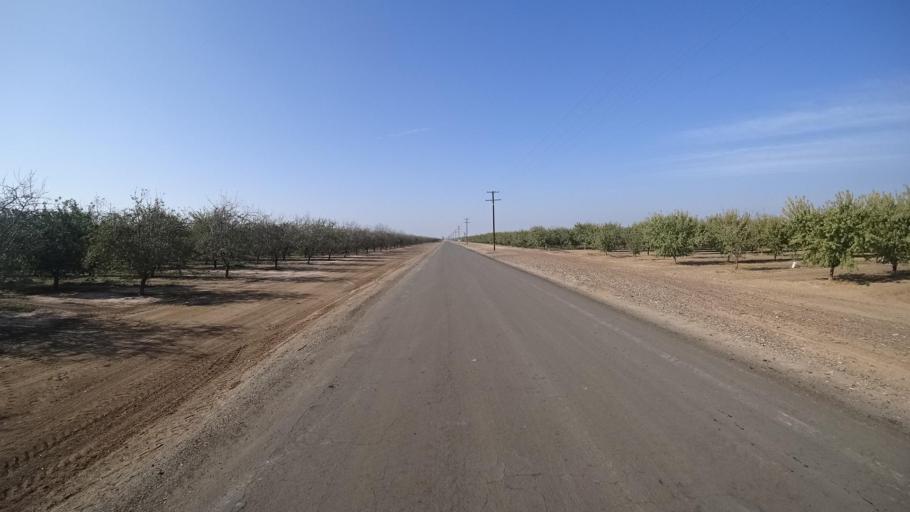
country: US
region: California
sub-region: Kern County
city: McFarland
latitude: 35.6601
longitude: -119.1833
